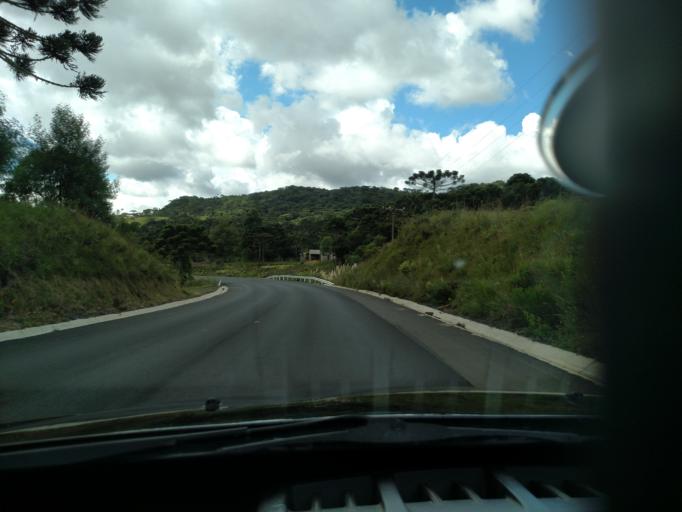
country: BR
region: Santa Catarina
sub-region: Lages
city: Lages
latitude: -27.9403
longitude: -50.0943
